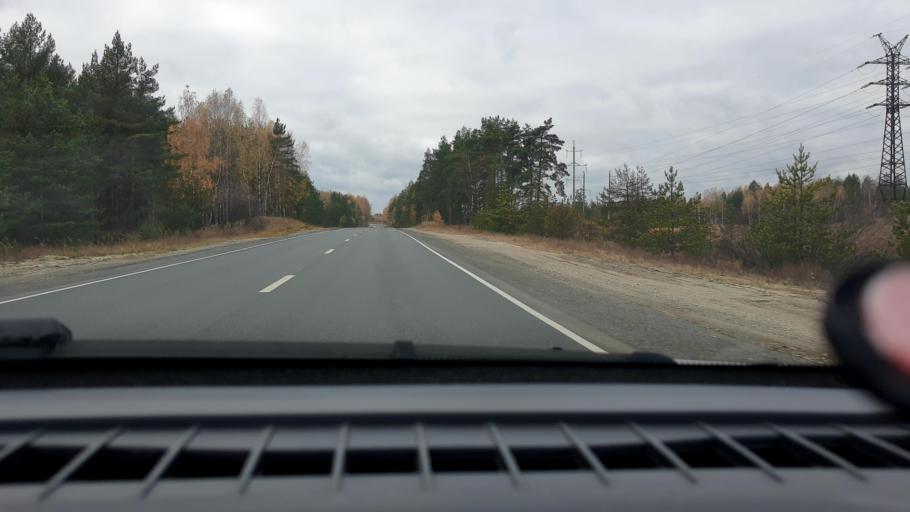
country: RU
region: Nizjnij Novgorod
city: Lukino
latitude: 56.3634
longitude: 43.6053
